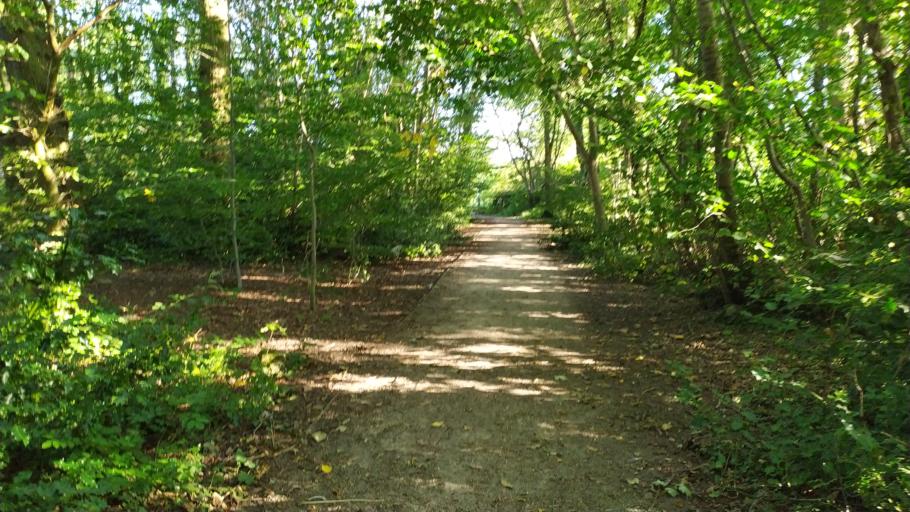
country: GB
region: England
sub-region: City and Borough of Leeds
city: Chapel Allerton
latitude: 53.8336
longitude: -1.5581
